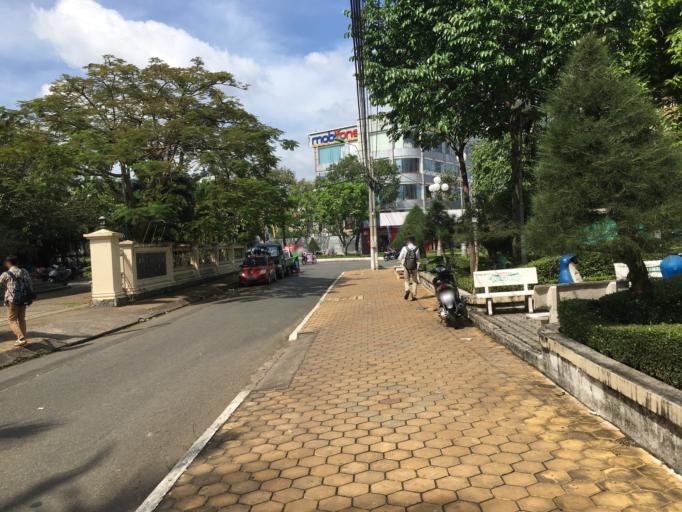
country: VN
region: Can Tho
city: Can Tho
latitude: 10.0353
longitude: 105.7871
